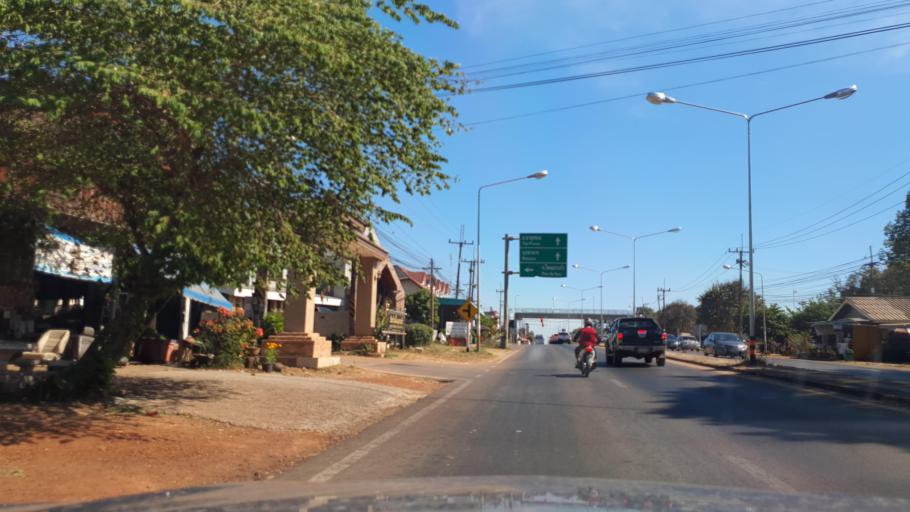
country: TH
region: Sakon Nakhon
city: Sakon Nakhon
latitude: 17.0840
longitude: 104.1891
